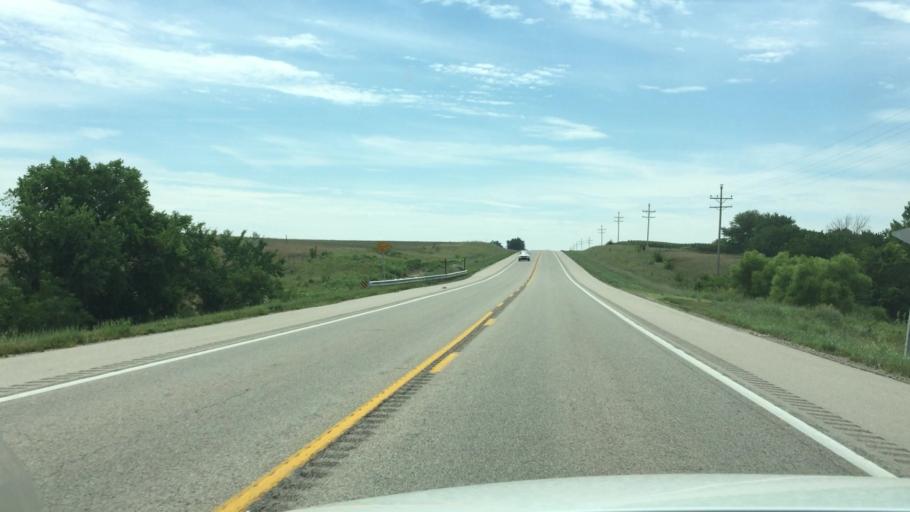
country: US
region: Kansas
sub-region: Nemaha County
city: Sabetha
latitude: 39.7927
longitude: -95.7295
